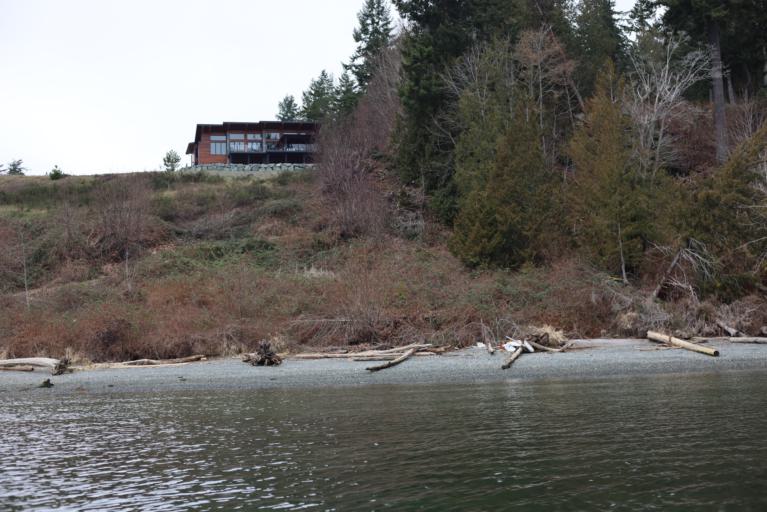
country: CA
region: British Columbia
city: North Saanich
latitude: 48.6680
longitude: -123.5314
